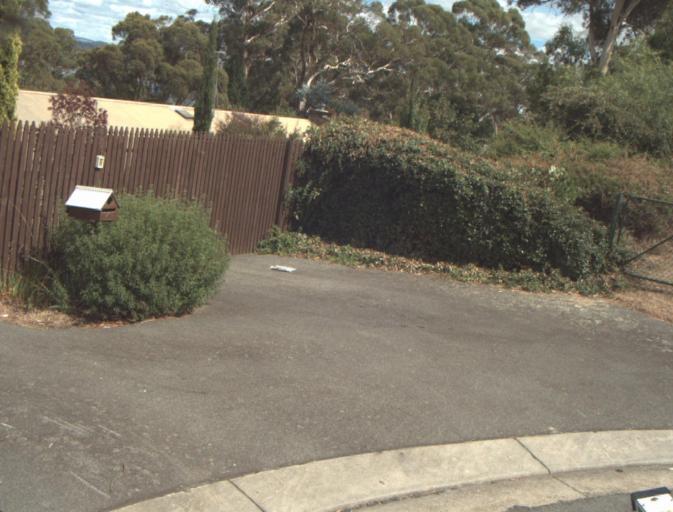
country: AU
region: Tasmania
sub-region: Launceston
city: Mayfield
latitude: -41.3384
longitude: 147.0817
